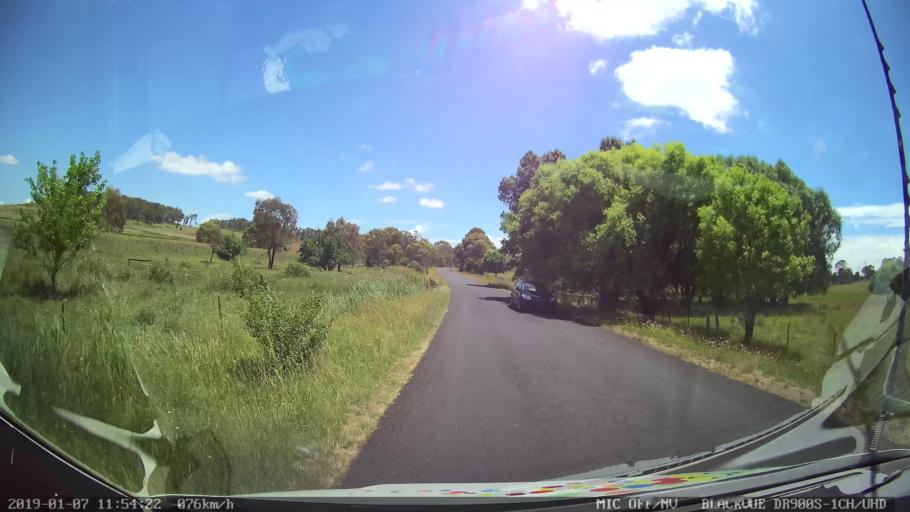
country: AU
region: New South Wales
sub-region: Guyra
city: Guyra
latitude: -30.2969
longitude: 151.6643
